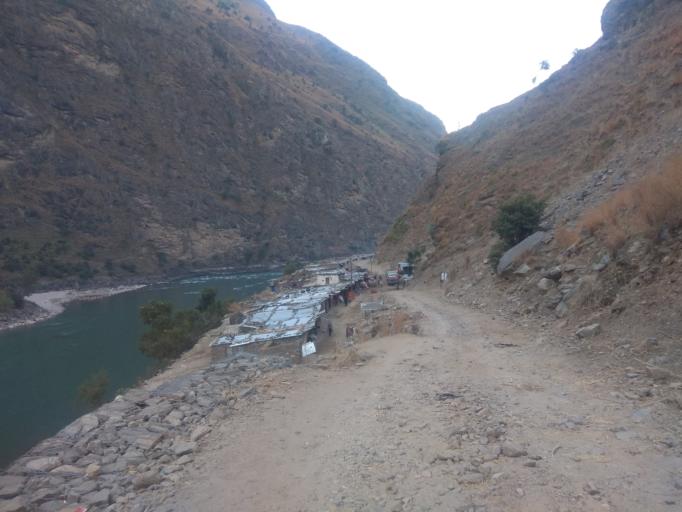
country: NP
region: Mid Western
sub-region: Bheri Zone
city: Dailekh
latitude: 29.2761
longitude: 81.7277
